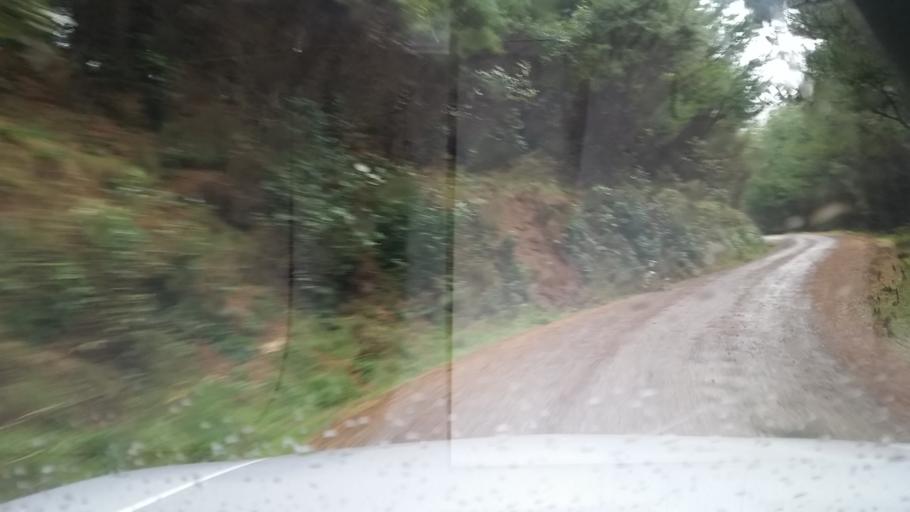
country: NZ
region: Marlborough
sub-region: Marlborough District
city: Picton
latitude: -41.1366
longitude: 174.0561
